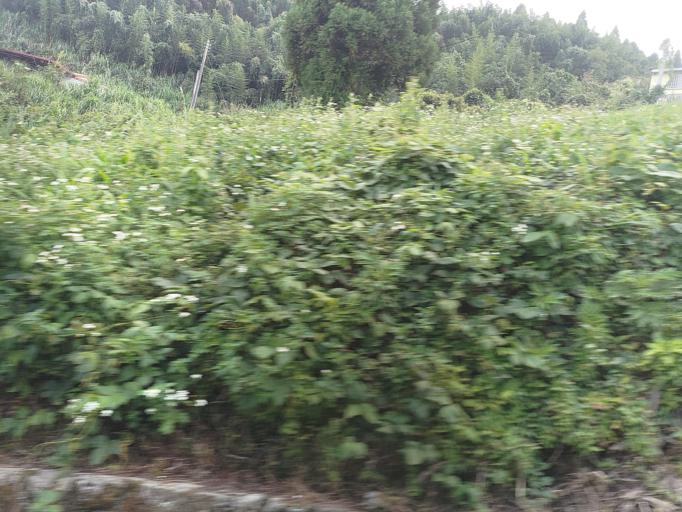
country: TW
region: Taiwan
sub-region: Hsinchu
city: Hsinchu
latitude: 24.6040
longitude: 121.0913
